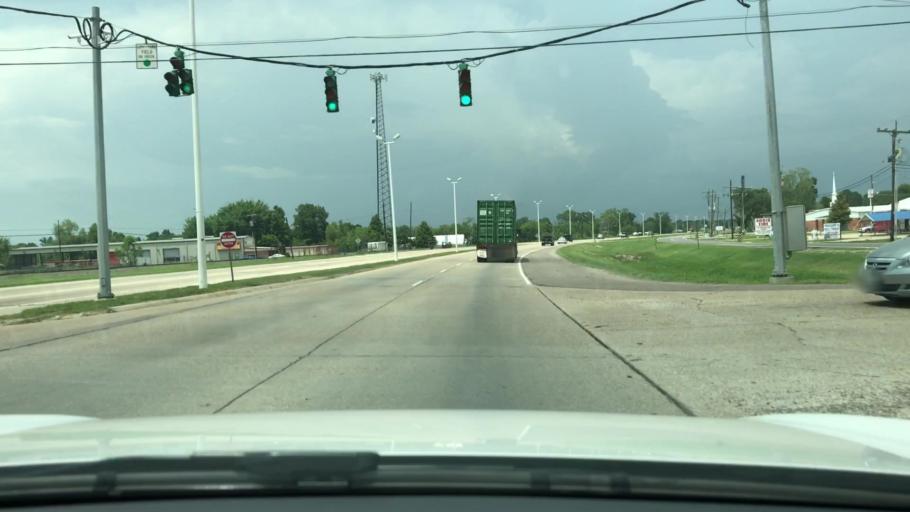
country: US
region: Louisiana
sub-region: West Baton Rouge Parish
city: Addis
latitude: 30.3640
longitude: -91.2607
